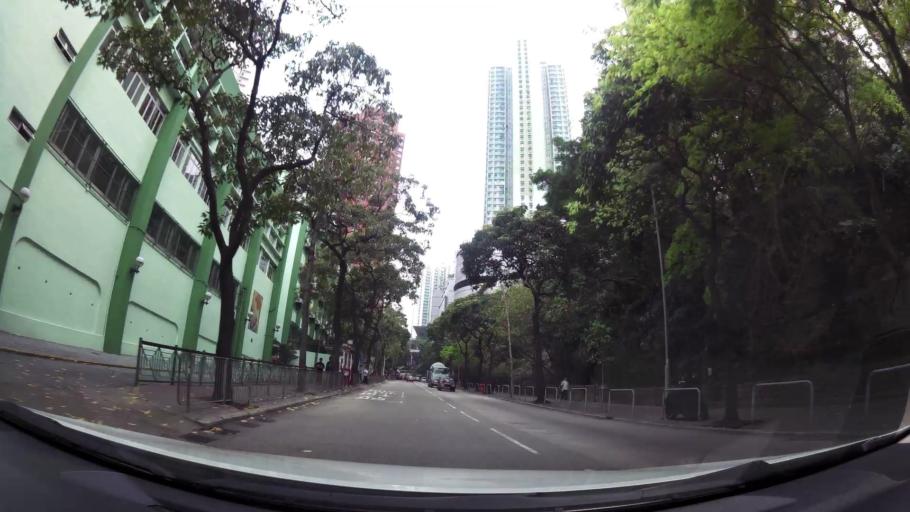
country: HK
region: Kowloon City
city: Kowloon
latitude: 22.3060
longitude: 114.2355
